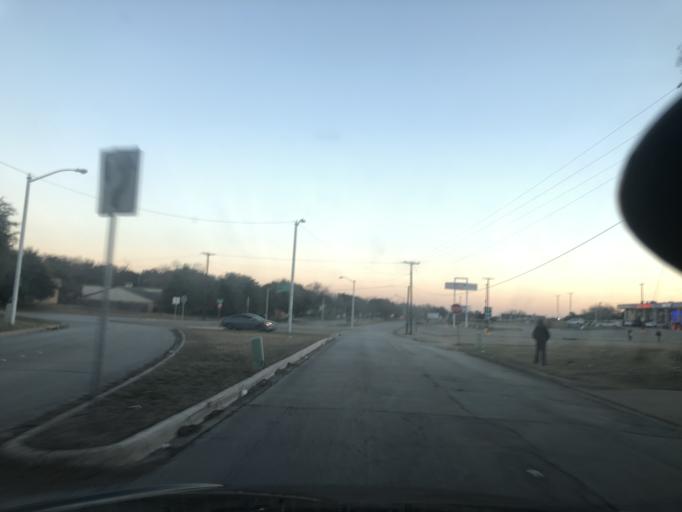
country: US
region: Texas
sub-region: Tarrant County
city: White Settlement
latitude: 32.7299
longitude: -97.4675
